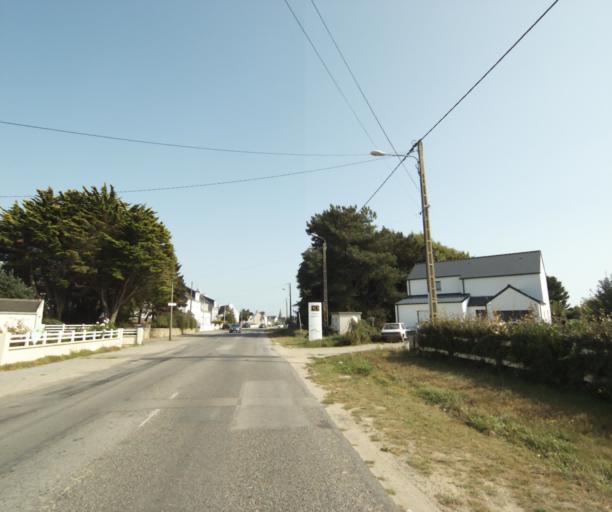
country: FR
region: Brittany
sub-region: Departement du Morbihan
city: Merlevenez
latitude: 47.7018
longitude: -3.2590
